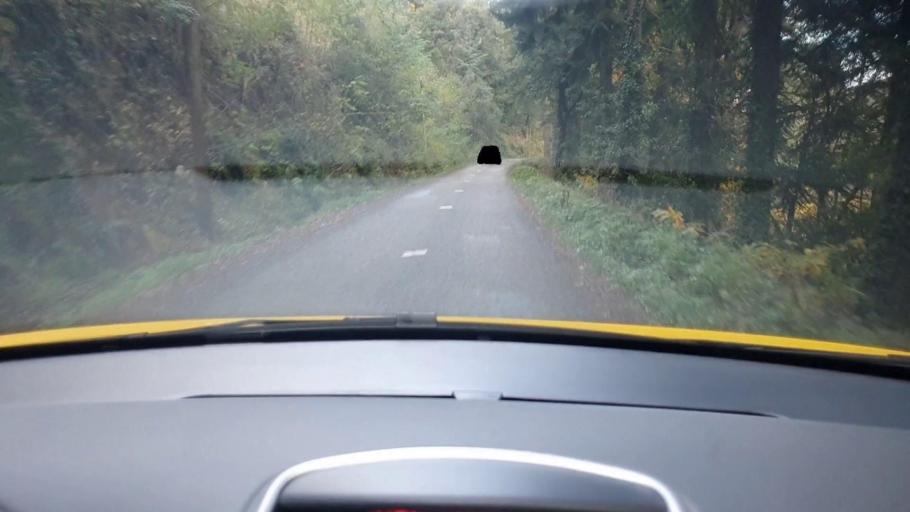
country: FR
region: Languedoc-Roussillon
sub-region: Departement du Gard
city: Lasalle
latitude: 44.0844
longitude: 3.8016
